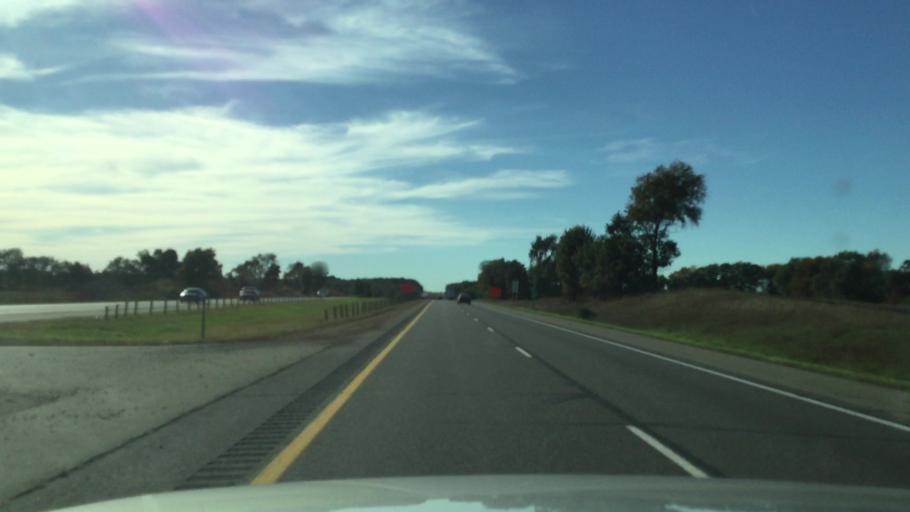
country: US
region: Michigan
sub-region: Calhoun County
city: Albion
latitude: 42.2838
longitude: -84.8105
